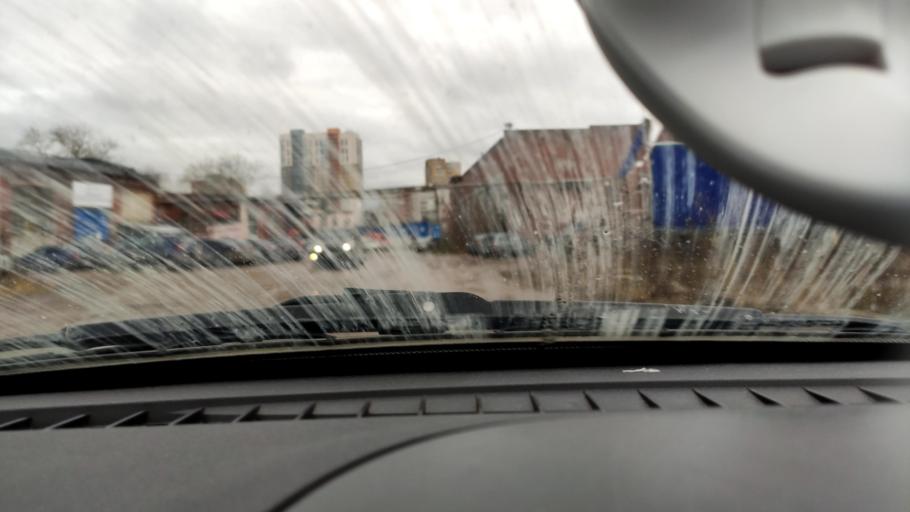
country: RU
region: Perm
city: Kondratovo
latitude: 58.0033
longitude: 56.1462
